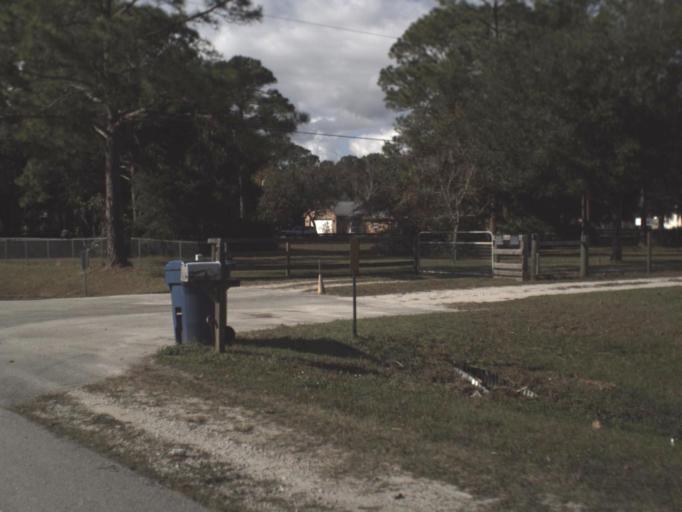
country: US
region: Florida
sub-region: Volusia County
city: Samsula-Spruce Creek
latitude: 29.0844
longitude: -81.0597
